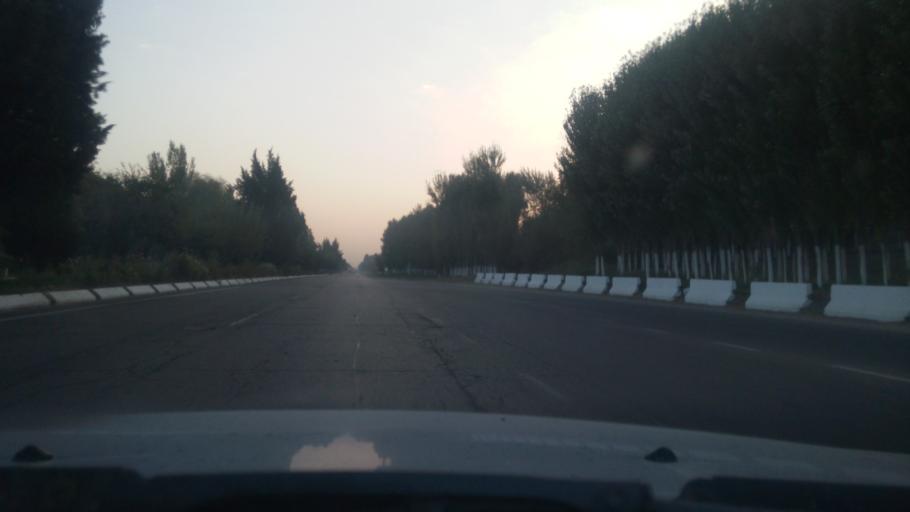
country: UZ
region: Toshkent
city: Amir Timur
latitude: 41.0535
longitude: 68.8998
